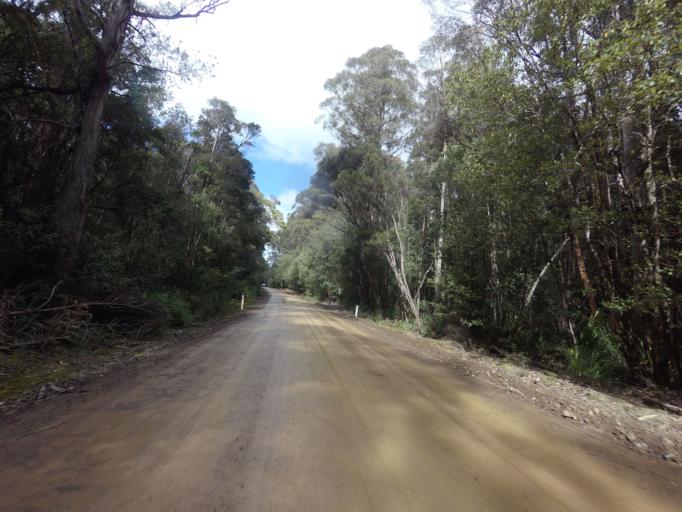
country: AU
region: Tasmania
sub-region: Huon Valley
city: Geeveston
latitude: -43.4105
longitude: 146.8727
